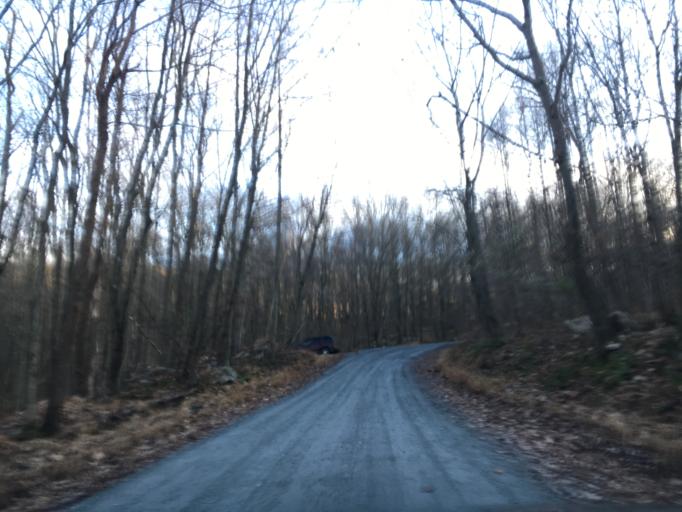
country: US
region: Pennsylvania
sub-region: Carbon County
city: Lehighton
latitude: 40.7707
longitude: -75.6985
